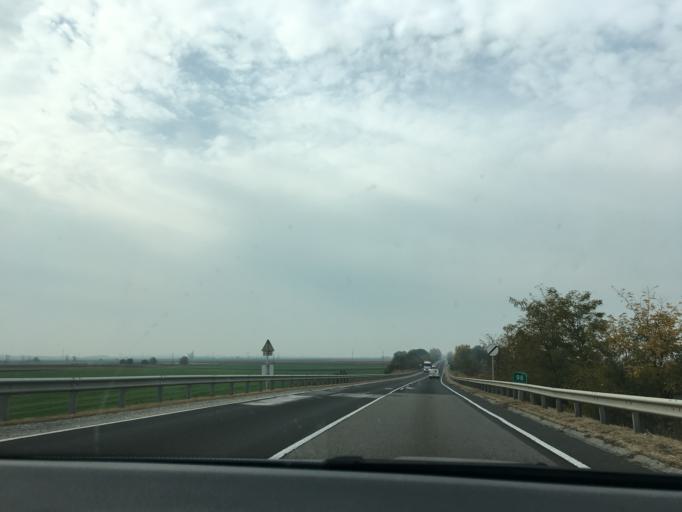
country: HU
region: Jasz-Nagykun-Szolnok
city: Toszeg
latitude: 47.1518
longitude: 20.1313
